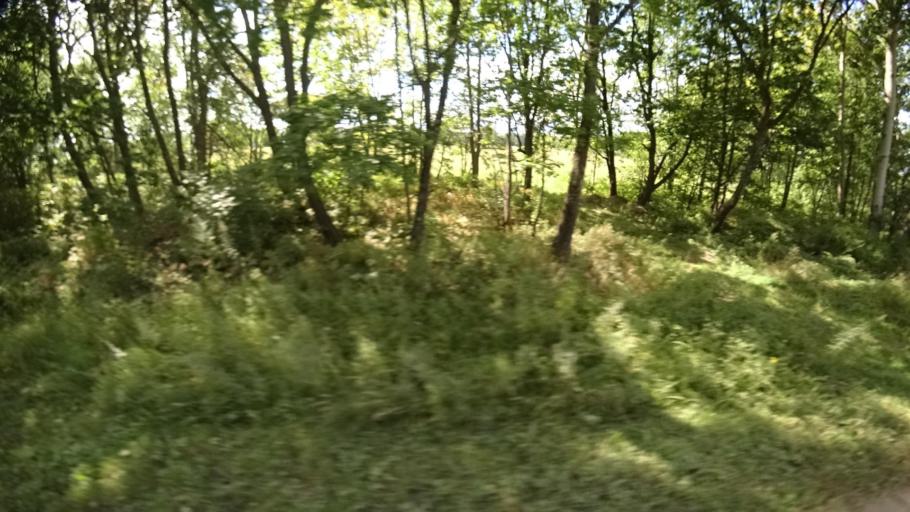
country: RU
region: Primorskiy
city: Yakovlevka
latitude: 44.4154
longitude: 133.5704
